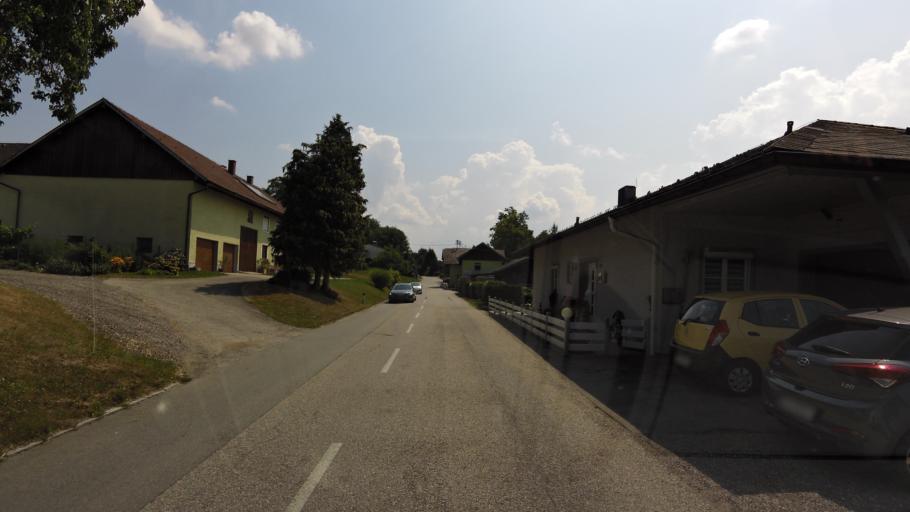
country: AT
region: Upper Austria
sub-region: Politischer Bezirk Ried im Innkreis
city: Waldzell
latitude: 48.1709
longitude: 13.4145
